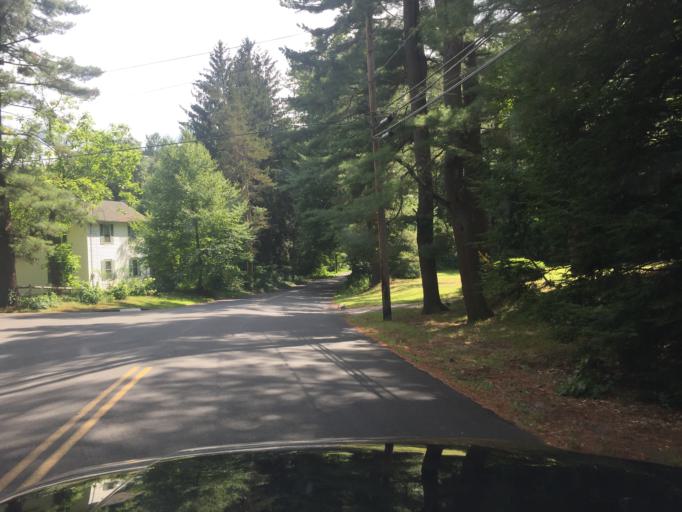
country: US
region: Connecticut
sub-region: Hartford County
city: Salmon Brook
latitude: 41.9591
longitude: -72.7836
